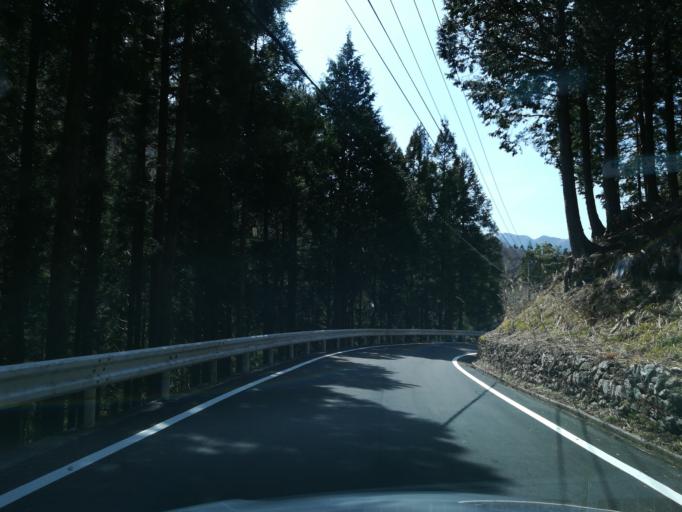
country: JP
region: Tokushima
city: Wakimachi
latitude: 33.8580
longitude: 134.0584
